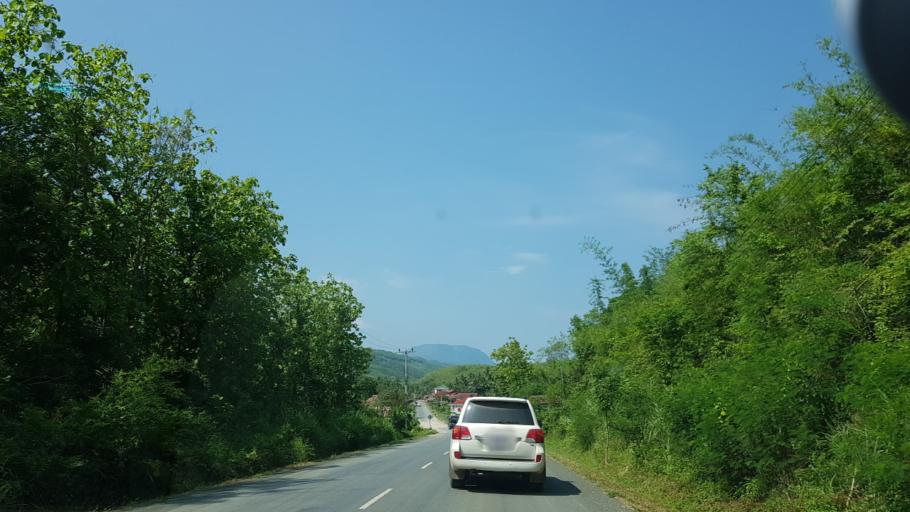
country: LA
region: Louangphabang
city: Xiang Ngeun
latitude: 19.7347
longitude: 102.1564
